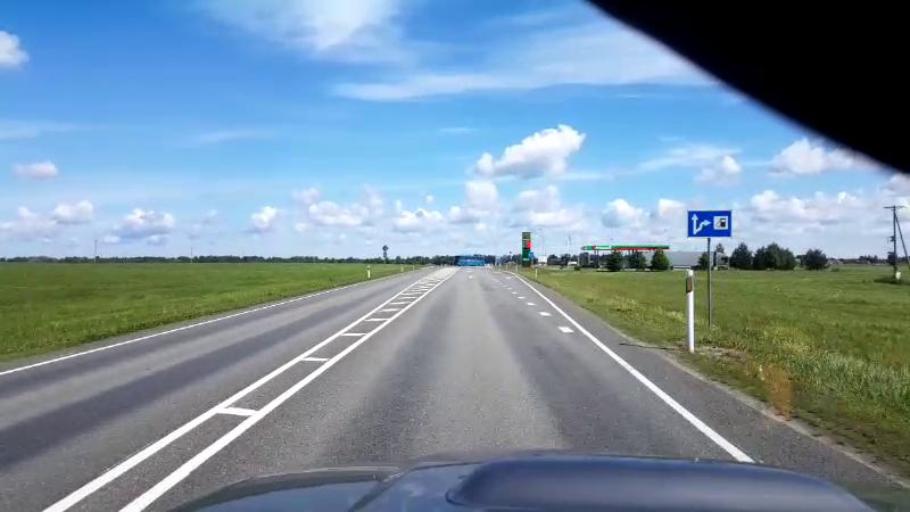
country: EE
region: Jaervamaa
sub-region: Jaerva-Jaani vald
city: Jarva-Jaani
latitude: 59.1778
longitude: 25.7597
